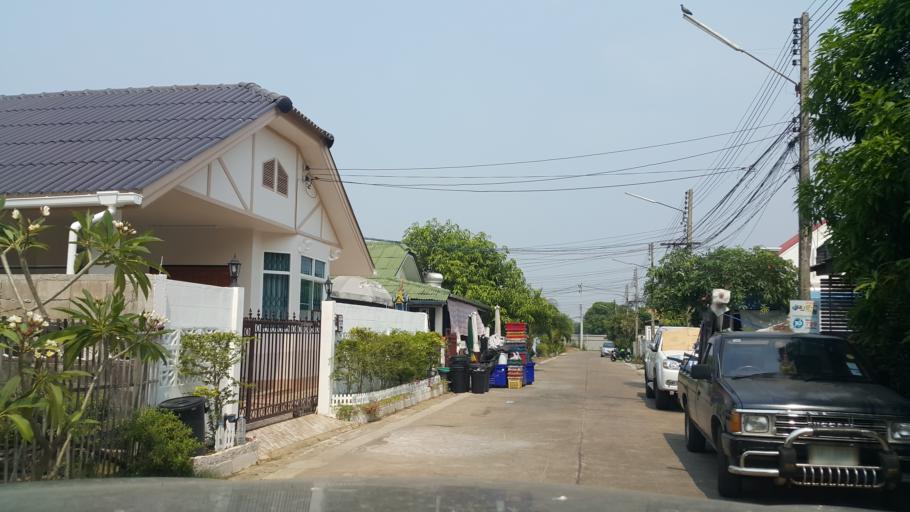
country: TH
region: Chiang Mai
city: Chiang Mai
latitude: 18.7862
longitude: 98.9607
